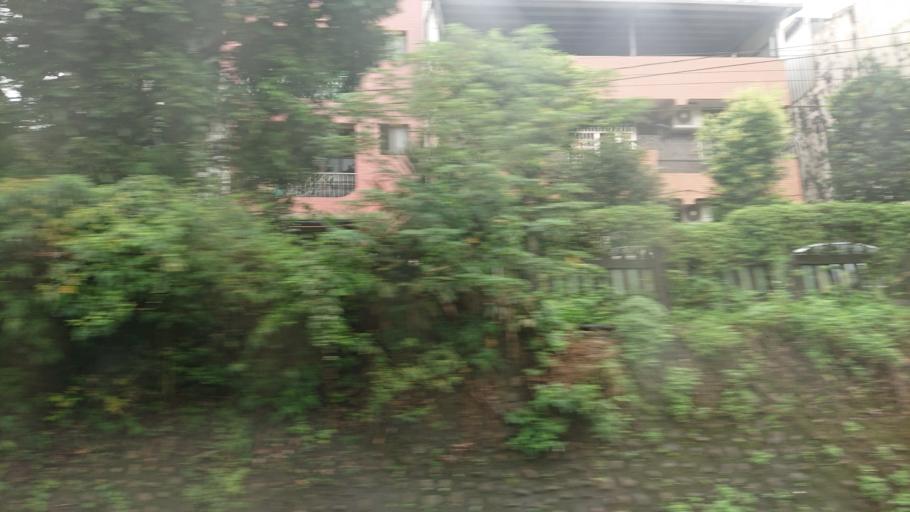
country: TW
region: Taiwan
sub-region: Keelung
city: Keelung
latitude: 25.0853
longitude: 121.7055
